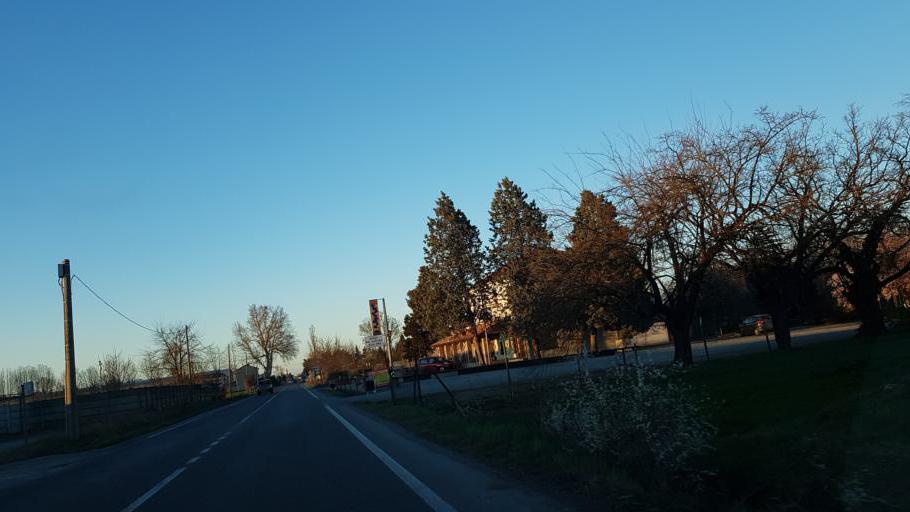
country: IT
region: Piedmont
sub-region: Provincia di Alessandria
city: Carbonara Scrivia
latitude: 44.8613
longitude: 8.8554
